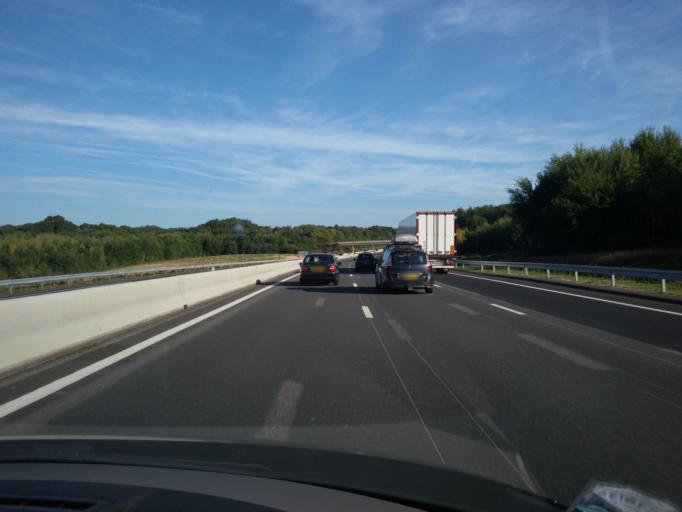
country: FR
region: Centre
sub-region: Departement du Loir-et-Cher
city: Theillay
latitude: 47.2602
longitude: 2.0452
